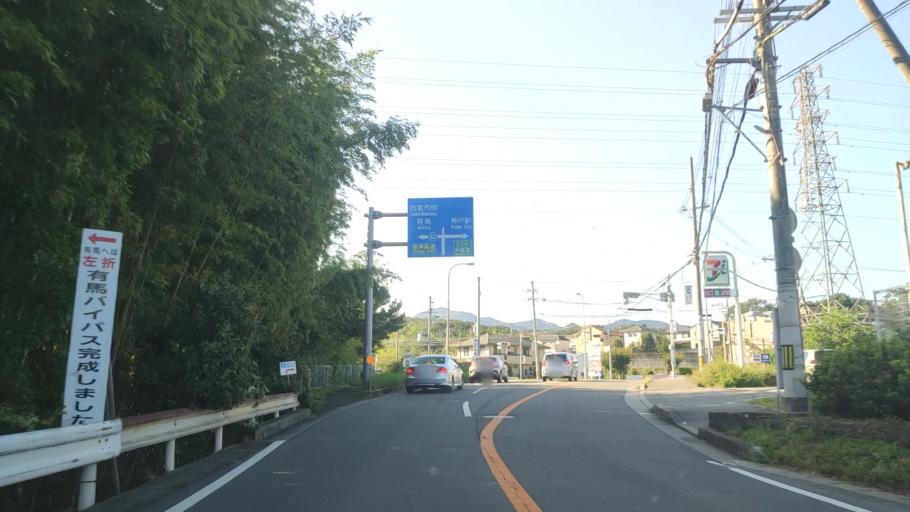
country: JP
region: Hyogo
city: Sandacho
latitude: 34.8215
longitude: 135.2466
